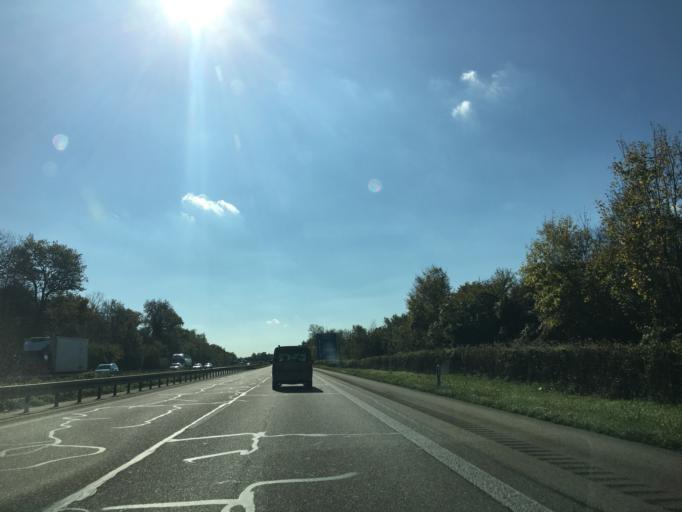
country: DE
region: Baden-Wuerttemberg
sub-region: Freiburg Region
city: Hartheim
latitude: 47.9150
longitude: 7.5922
